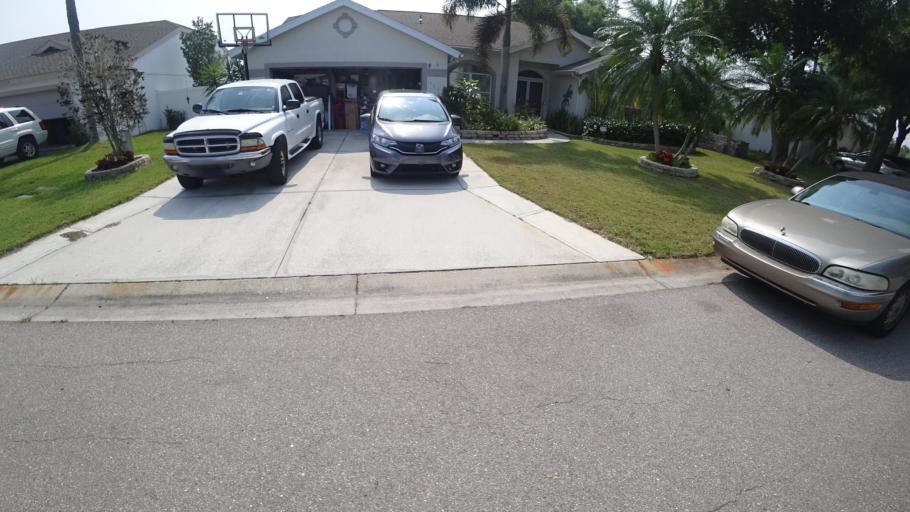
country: US
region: Florida
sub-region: Manatee County
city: Samoset
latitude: 27.4599
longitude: -82.5111
